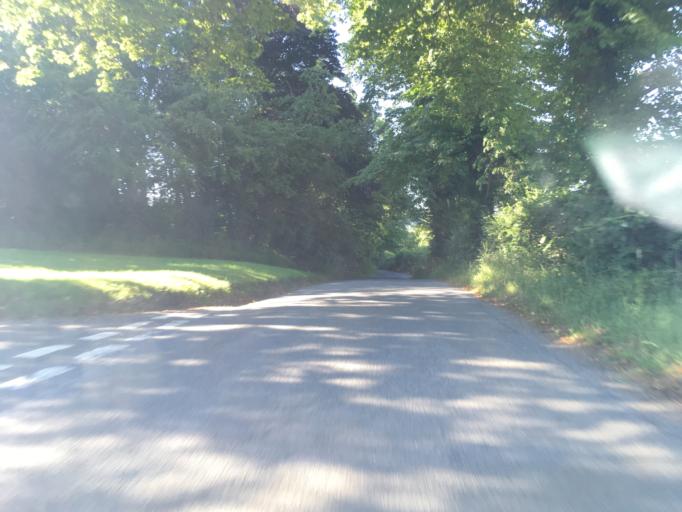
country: GB
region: England
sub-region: South Gloucestershire
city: Hinton
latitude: 51.4814
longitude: -2.3814
